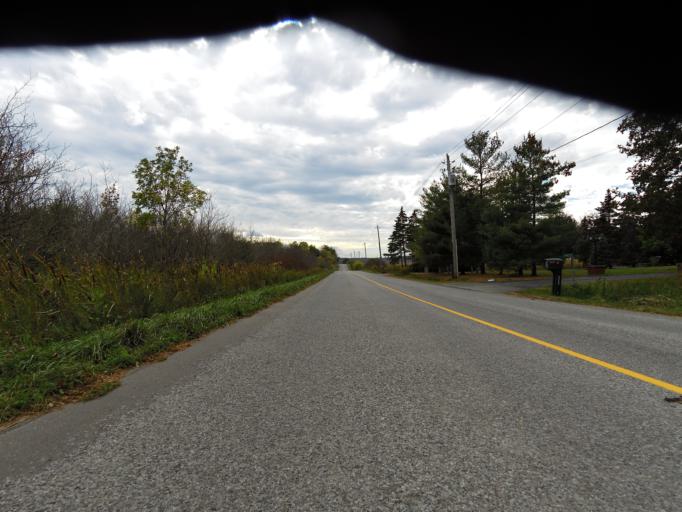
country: CA
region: Ontario
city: Burlington
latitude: 43.4169
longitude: -79.8301
